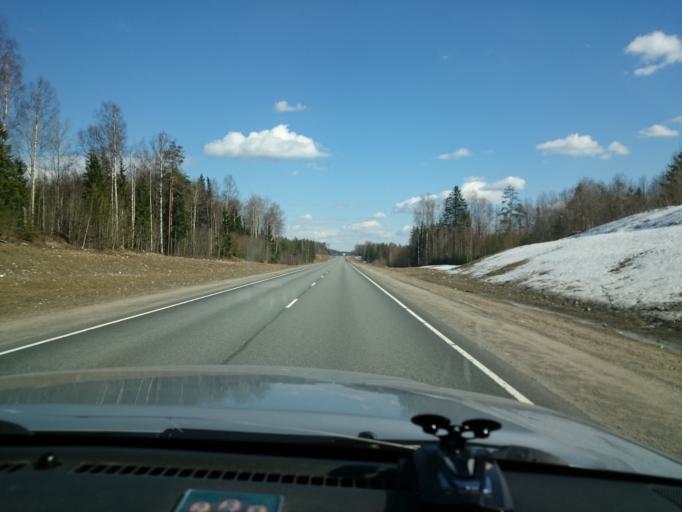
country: RU
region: Republic of Karelia
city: Pryazha
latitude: 61.5258
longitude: 33.4958
